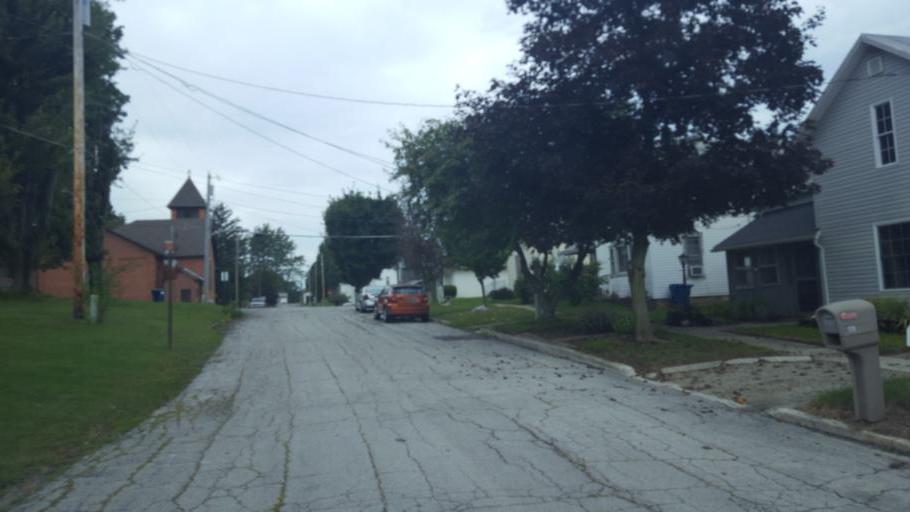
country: US
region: Ohio
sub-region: Seneca County
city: Tiffin
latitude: 40.9521
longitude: -83.1687
